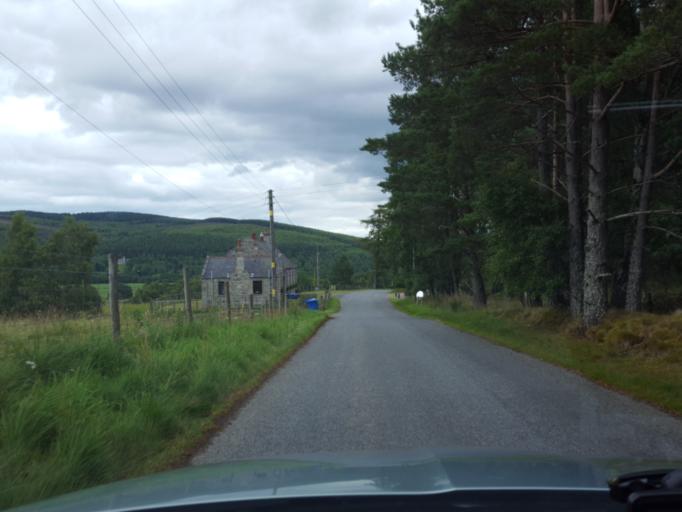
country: GB
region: Scotland
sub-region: Highland
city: Grantown on Spey
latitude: 57.3908
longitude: -3.4584
